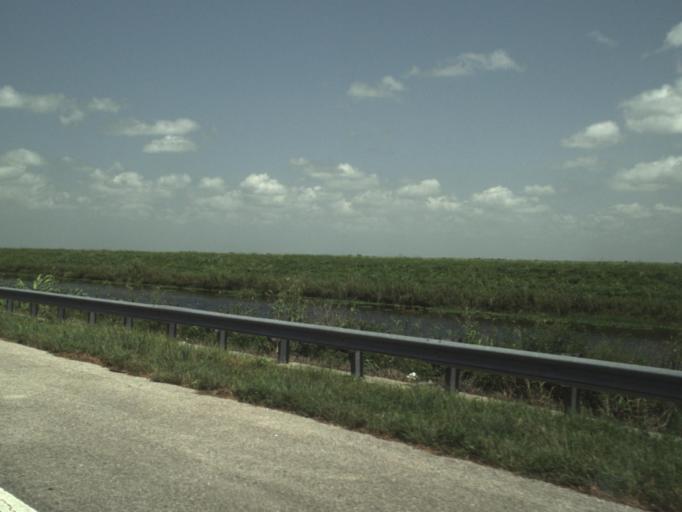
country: US
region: Florida
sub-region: Palm Beach County
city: Belle Glade Camp
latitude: 26.5198
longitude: -80.6809
